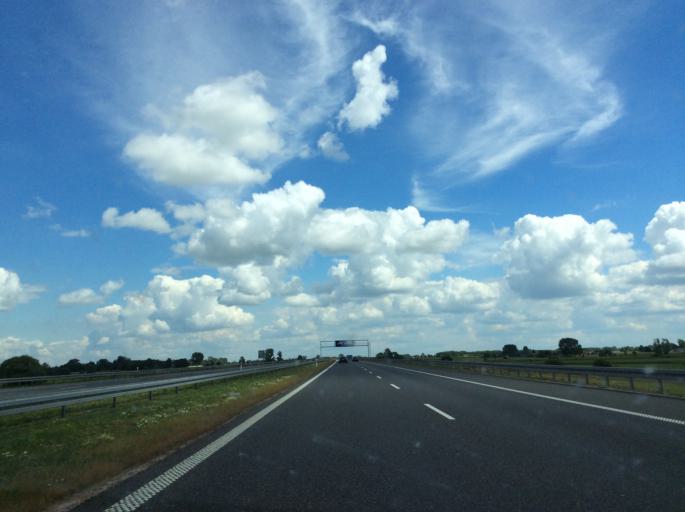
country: PL
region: Lodz Voivodeship
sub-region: Powiat poddebicki
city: Wartkowice
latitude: 51.9986
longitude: 19.0136
